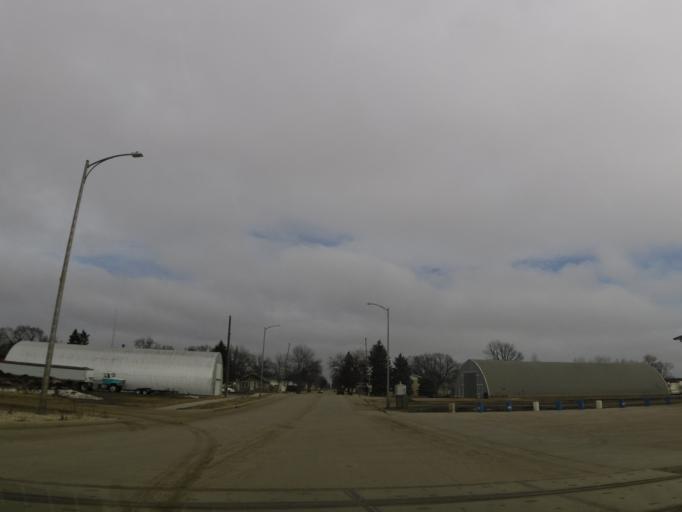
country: US
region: North Dakota
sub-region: Walsh County
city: Grafton
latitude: 48.4165
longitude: -97.4087
